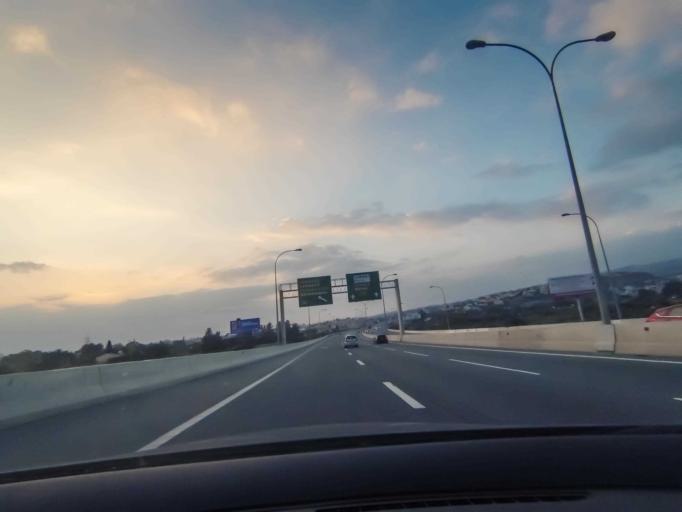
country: CY
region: Limassol
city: Mouttagiaka
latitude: 34.7062
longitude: 33.0949
